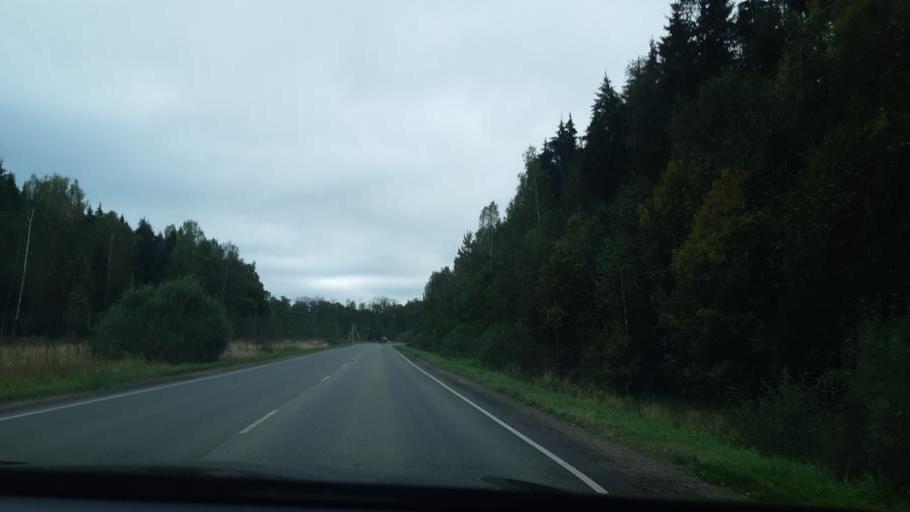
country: RU
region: Moskovskaya
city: Melikhovo
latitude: 55.1224
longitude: 37.6247
